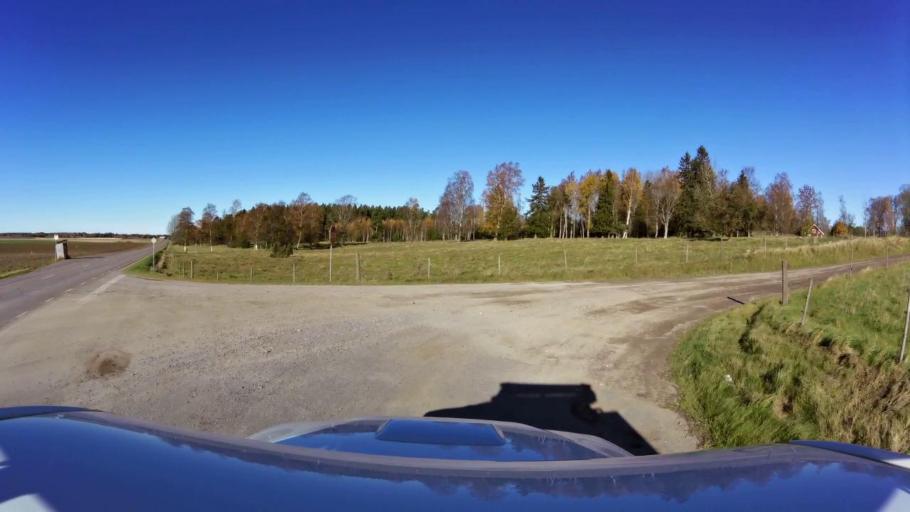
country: SE
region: OEstergoetland
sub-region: Linkopings Kommun
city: Vikingstad
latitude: 58.4830
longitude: 15.3877
